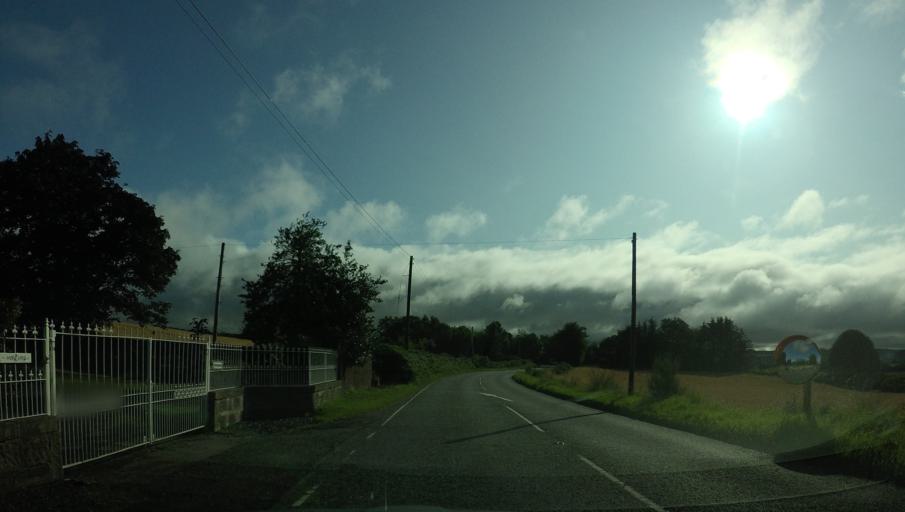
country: GB
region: Scotland
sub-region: Aberdeenshire
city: Banchory
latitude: 57.0600
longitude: -2.4093
